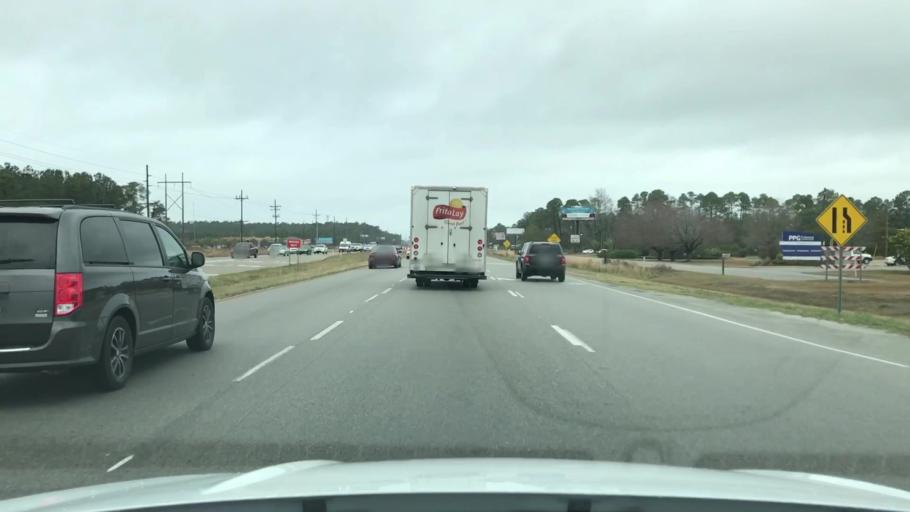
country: US
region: South Carolina
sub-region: Horry County
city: Red Hill
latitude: 33.7757
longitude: -78.9832
